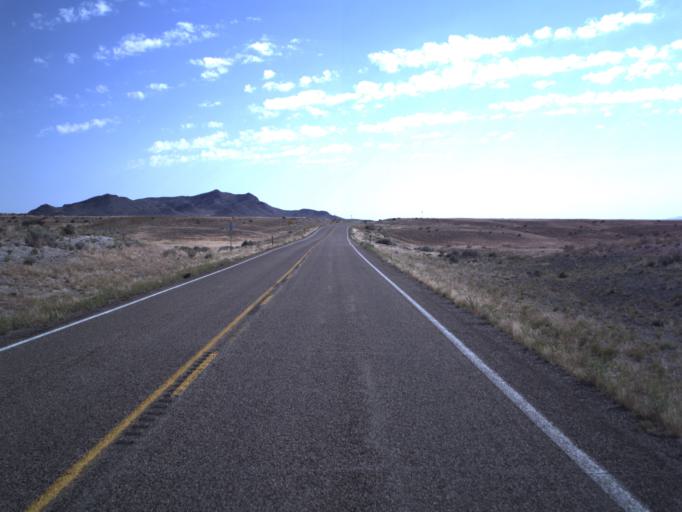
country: US
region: Utah
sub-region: Beaver County
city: Milford
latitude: 38.7833
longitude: -112.9214
